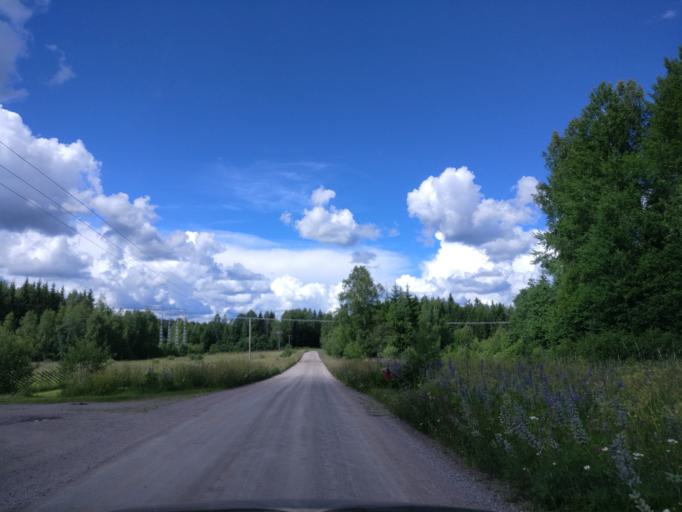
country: SE
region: Vaermland
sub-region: Hagfors Kommun
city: Hagfors
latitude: 60.0309
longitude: 13.6688
